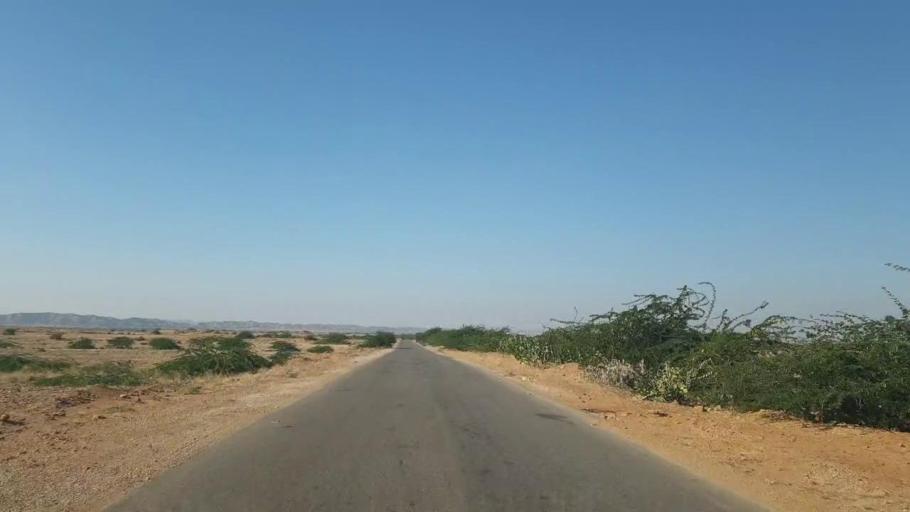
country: PK
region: Sindh
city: Malir Cantonment
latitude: 25.2714
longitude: 67.5923
